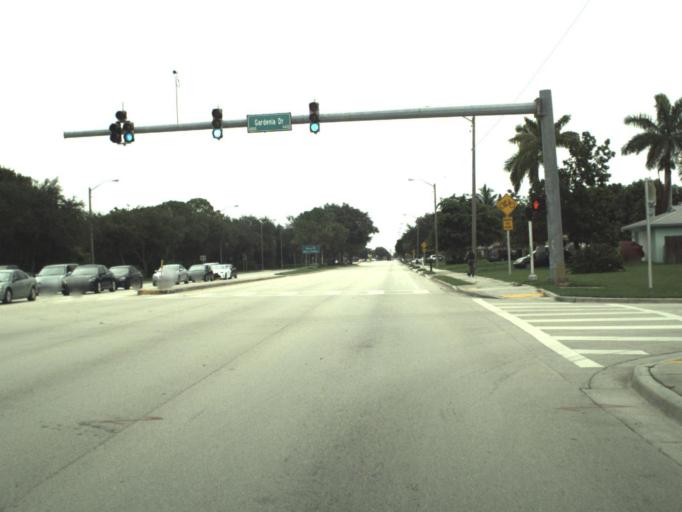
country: US
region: Florida
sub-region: Palm Beach County
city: North Palm Beach
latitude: 26.8185
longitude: -80.1059
